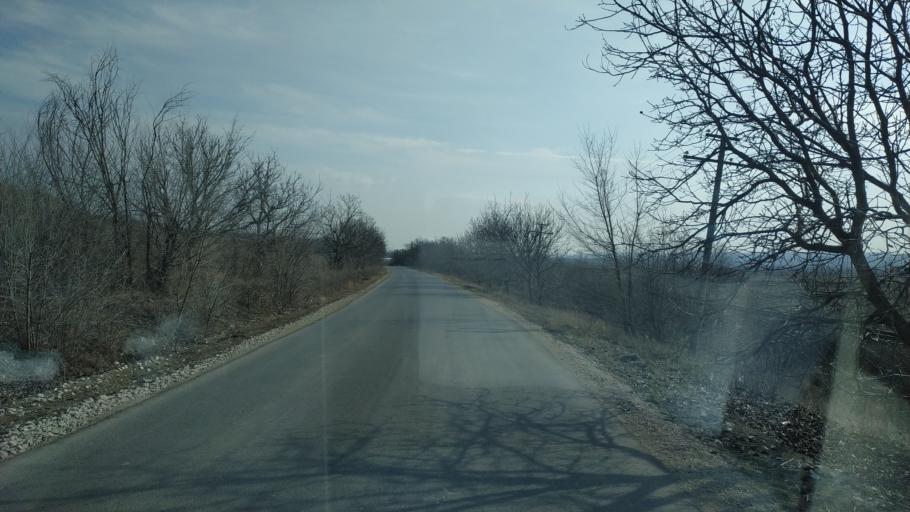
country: MD
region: Chisinau
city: Singera
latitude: 46.9192
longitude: 29.0997
